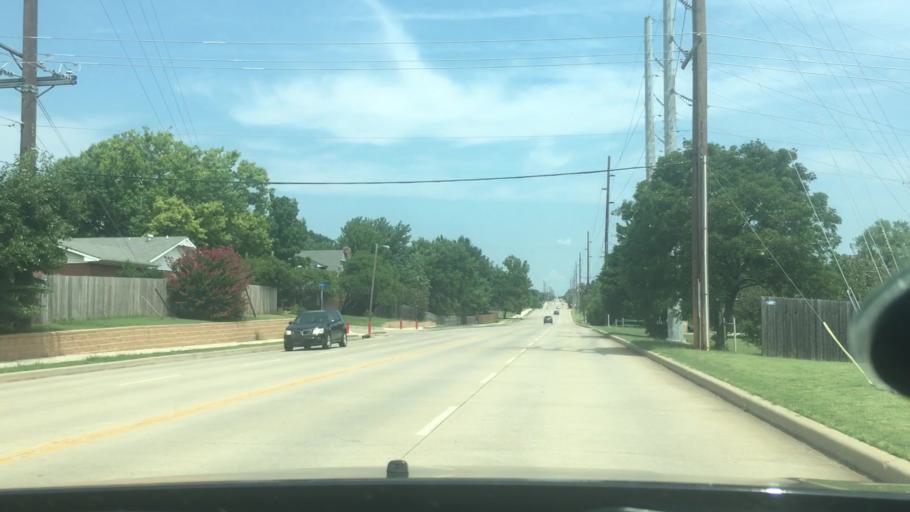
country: US
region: Oklahoma
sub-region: Pottawatomie County
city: Shawnee
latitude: 35.3397
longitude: -96.8943
